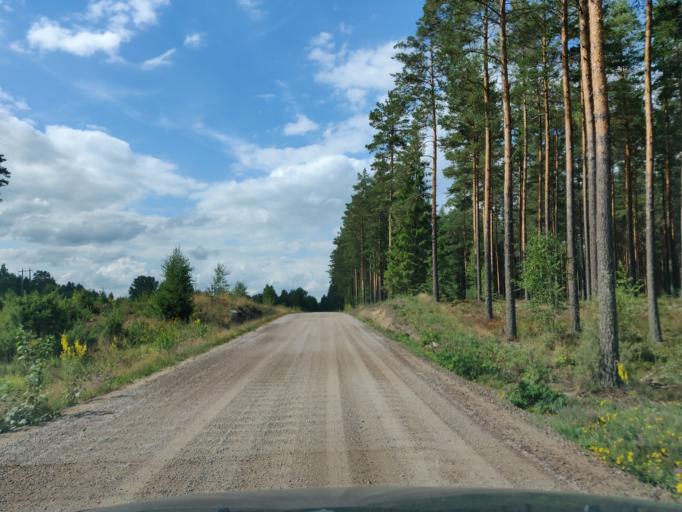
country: SE
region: Vaermland
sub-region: Munkfors Kommun
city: Munkfors
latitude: 59.9750
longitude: 13.5361
